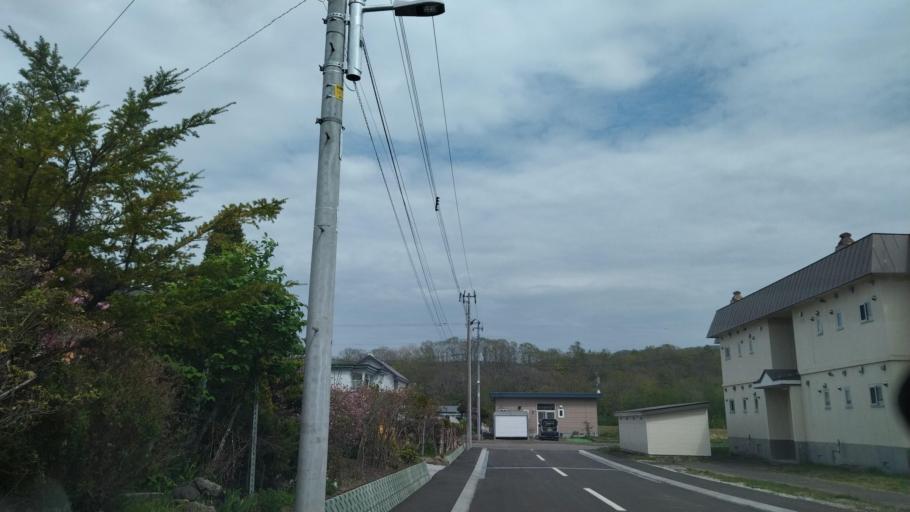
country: JP
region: Hokkaido
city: Otofuke
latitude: 43.2356
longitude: 143.5566
